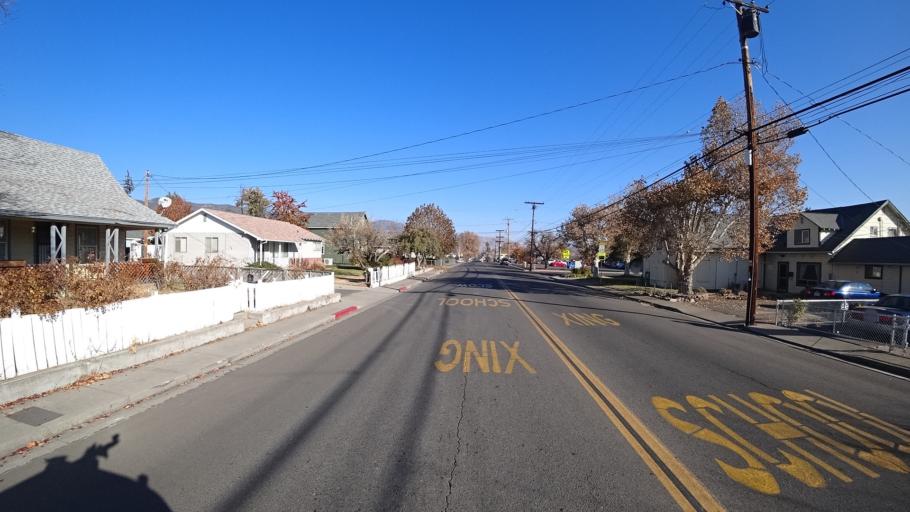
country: US
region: California
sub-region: Siskiyou County
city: Yreka
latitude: 41.7261
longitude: -122.6407
